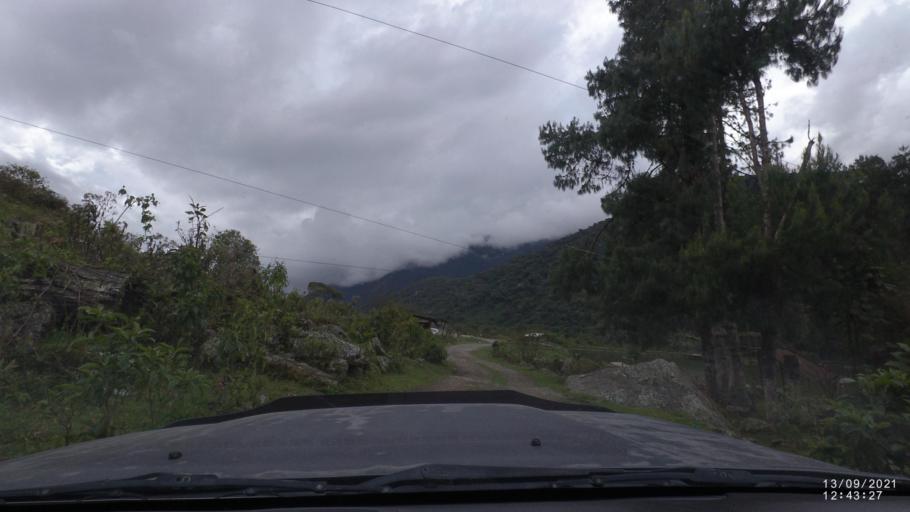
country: BO
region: Cochabamba
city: Colomi
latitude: -17.2539
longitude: -65.8177
